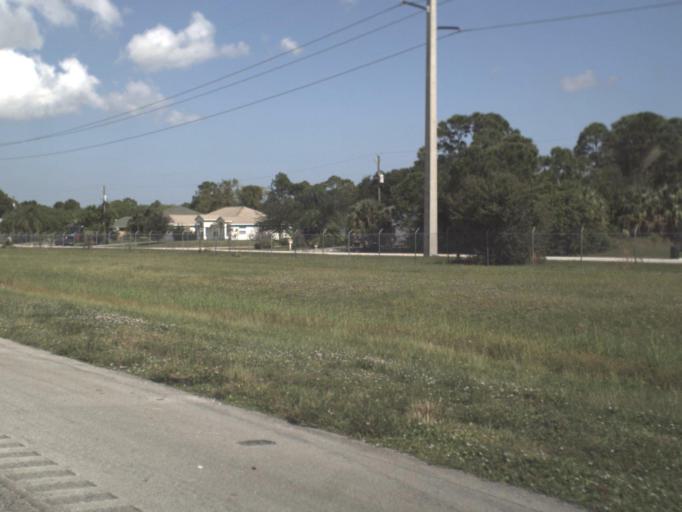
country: US
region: Florida
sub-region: Saint Lucie County
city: River Park
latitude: 27.3330
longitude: -80.3742
